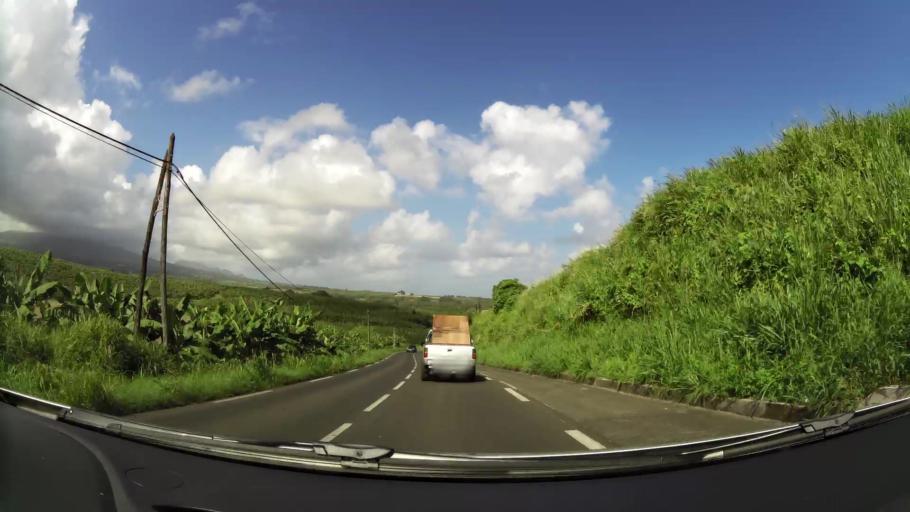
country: MQ
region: Martinique
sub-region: Martinique
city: Le Lorrain
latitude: 14.8398
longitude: -61.0798
